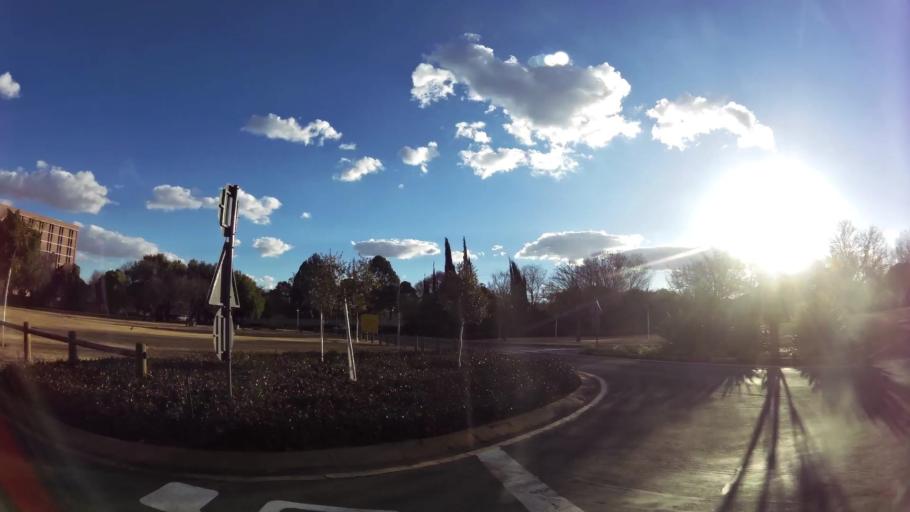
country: ZA
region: North-West
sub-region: Dr Kenneth Kaunda District Municipality
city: Potchefstroom
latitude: -26.6956
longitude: 27.0885
